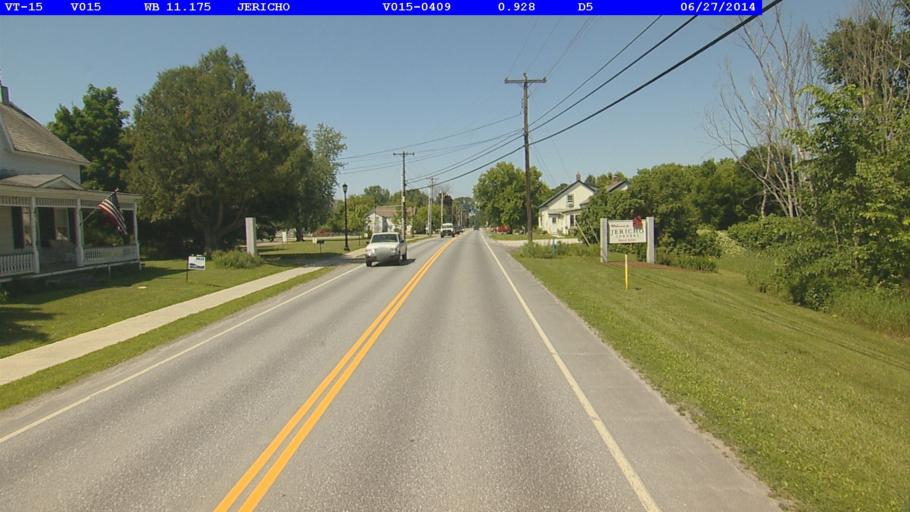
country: US
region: Vermont
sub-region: Chittenden County
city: Jericho
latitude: 44.5071
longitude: -72.9897
